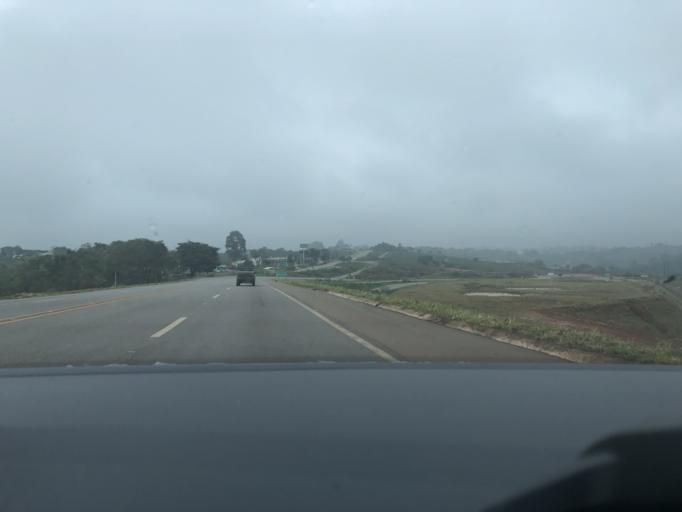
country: BR
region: Minas Gerais
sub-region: Congonhas
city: Congonhas
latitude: -20.6148
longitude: -43.9238
